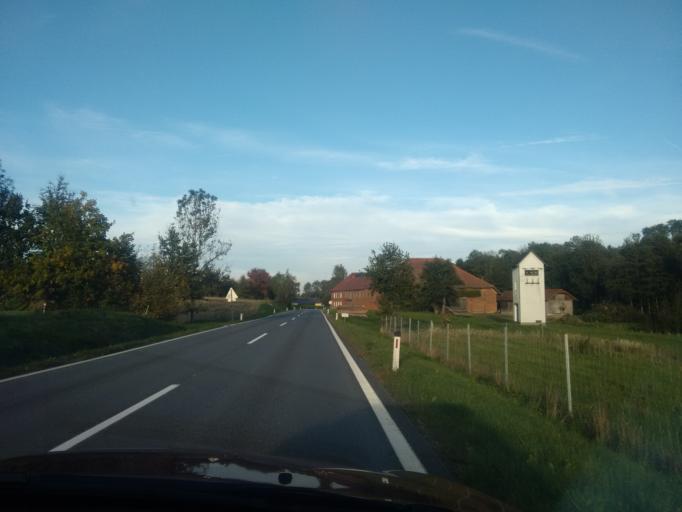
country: AT
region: Upper Austria
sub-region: Wels-Land
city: Bachmanning
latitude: 48.1695
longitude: 13.7551
